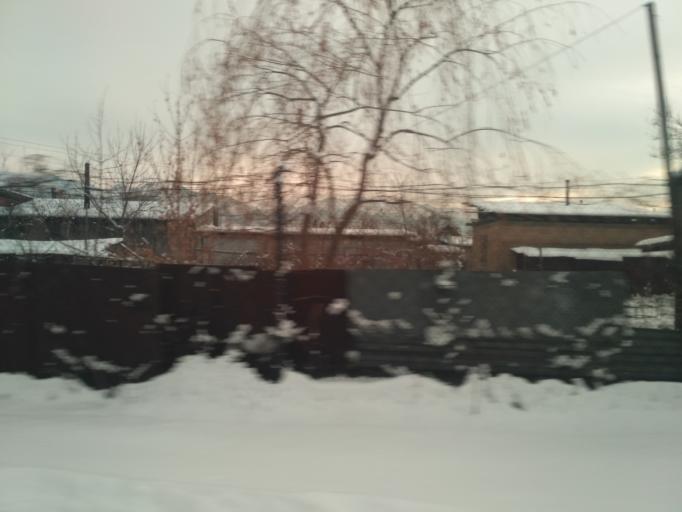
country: KZ
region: Almaty Qalasy
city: Almaty
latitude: 43.2116
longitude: 76.7826
